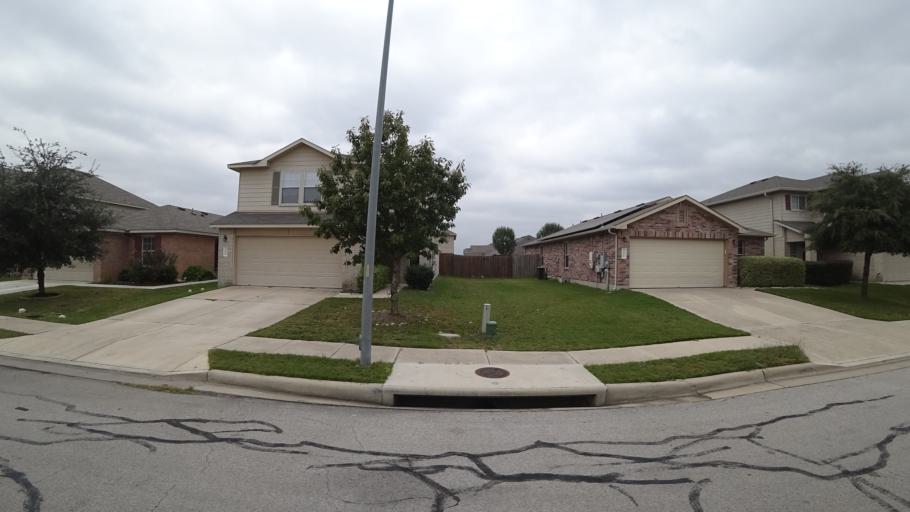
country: US
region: Texas
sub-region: Travis County
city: Pflugerville
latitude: 30.3896
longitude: -97.6182
